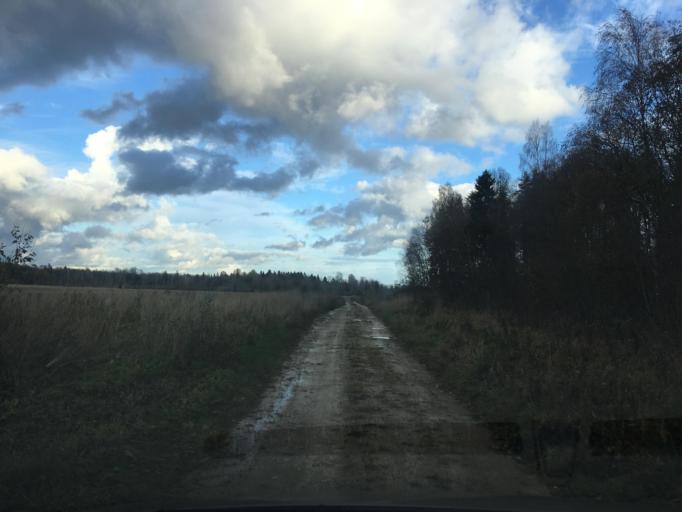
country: EE
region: Harju
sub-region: Raasiku vald
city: Arukula
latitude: 59.3588
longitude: 25.0988
